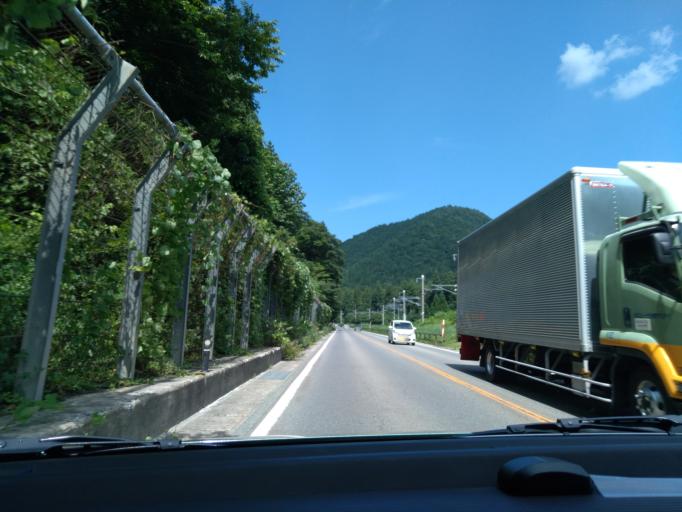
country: JP
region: Akita
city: Kakunodatemachi
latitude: 39.6432
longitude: 140.6613
